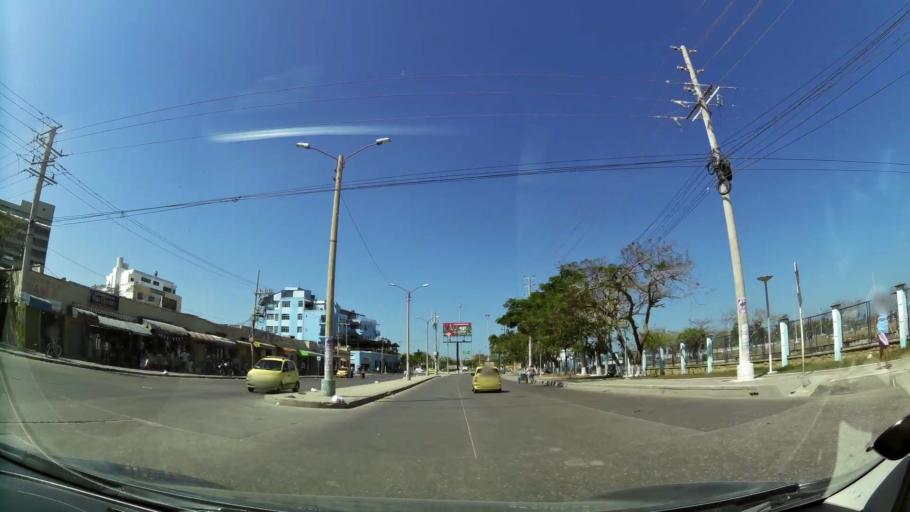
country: CO
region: Atlantico
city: Barranquilla
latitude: 10.9836
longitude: -74.7758
